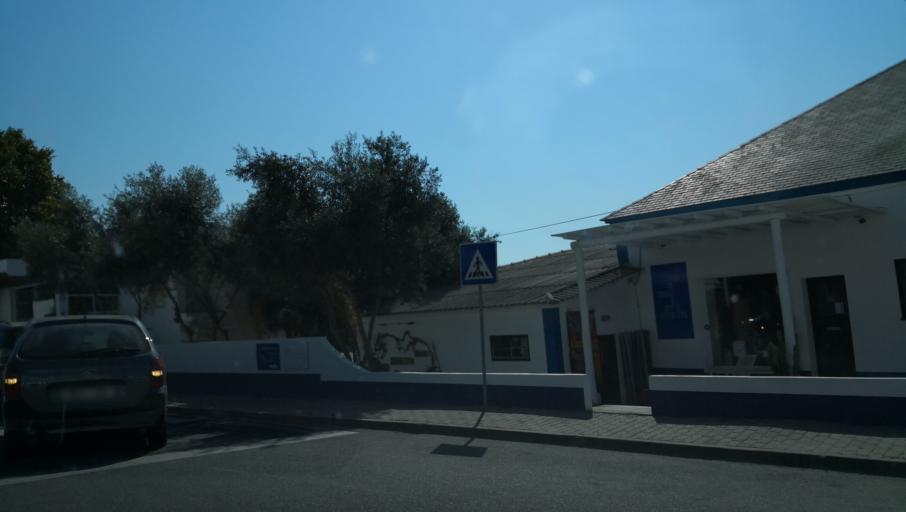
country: PT
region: Setubal
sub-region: Setubal
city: Setubal
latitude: 38.3814
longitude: -8.7876
